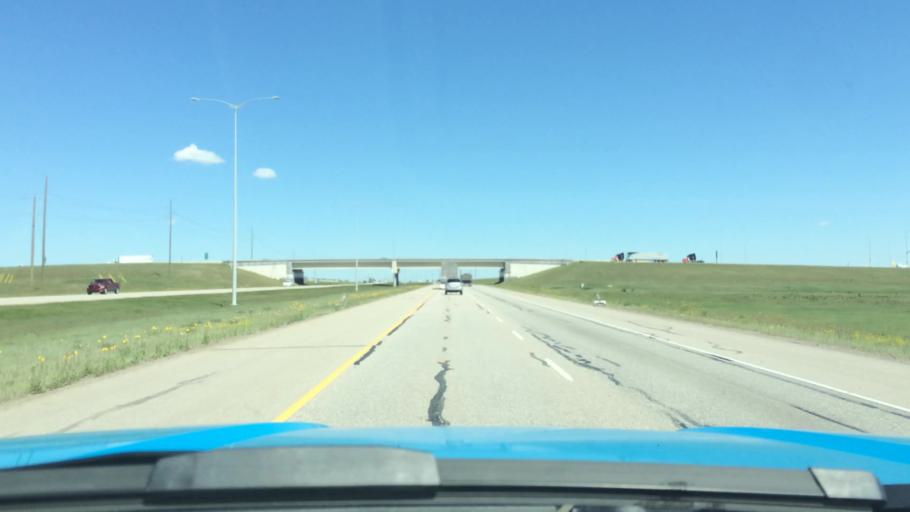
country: CA
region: Alberta
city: Chestermere
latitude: 51.0937
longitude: -113.9186
